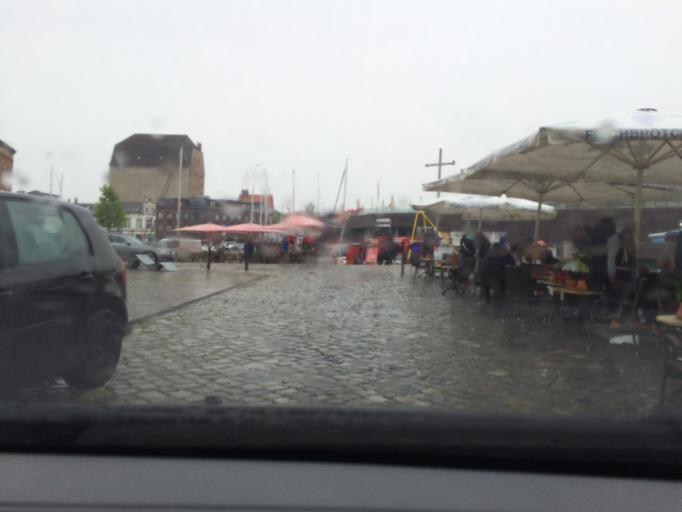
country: DE
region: Mecklenburg-Vorpommern
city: Stralsund
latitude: 54.3152
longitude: 13.0966
